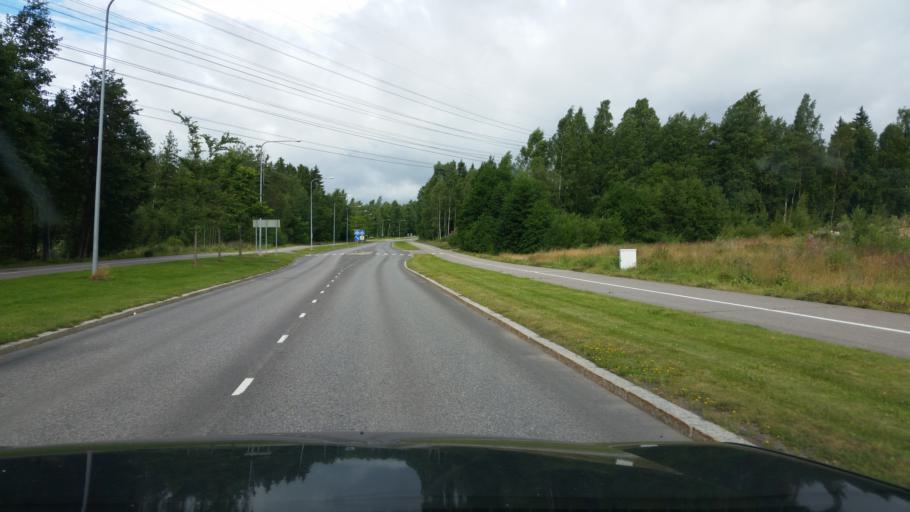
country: FI
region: Uusimaa
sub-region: Helsinki
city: Vantaa
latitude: 60.2207
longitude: 25.1595
